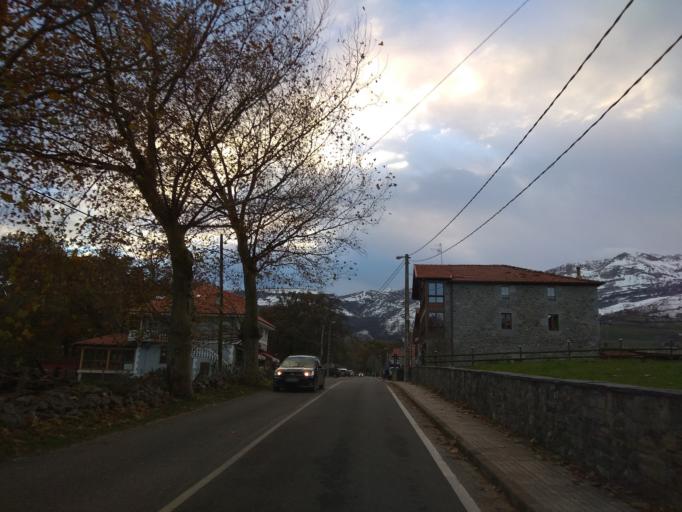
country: ES
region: Cantabria
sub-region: Provincia de Cantabria
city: Arredondo
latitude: 43.1921
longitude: -3.5690
